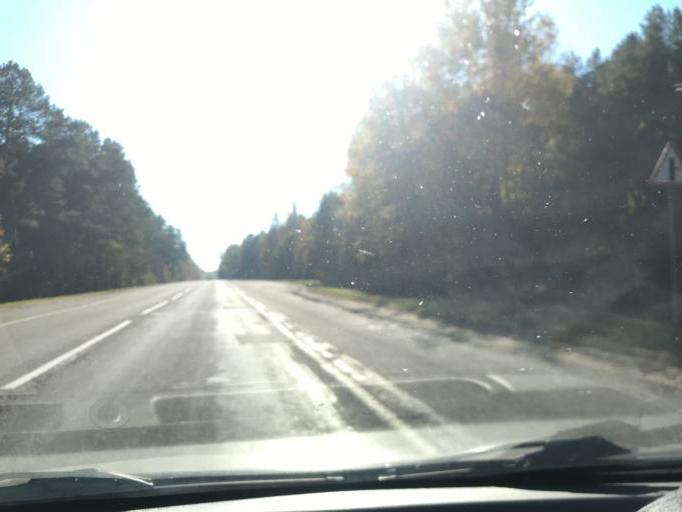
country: BY
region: Gomel
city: Kastsyukowka
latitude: 52.4330
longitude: 30.8269
